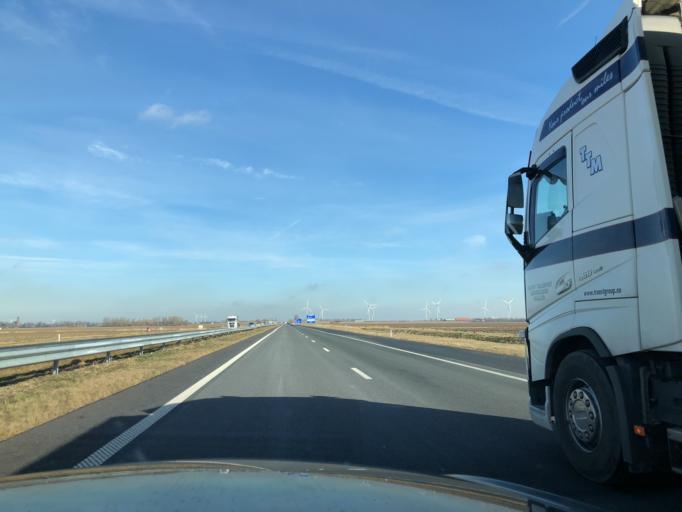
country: NL
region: North Brabant
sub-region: Gemeente Steenbergen
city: Dinteloord
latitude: 51.6110
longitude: 4.3726
